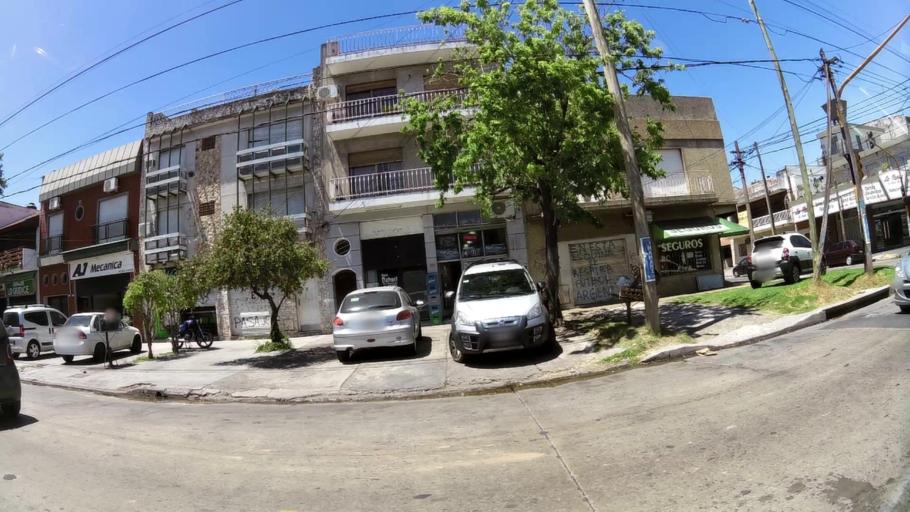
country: AR
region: Buenos Aires
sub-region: Partido de General San Martin
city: General San Martin
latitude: -34.5673
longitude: -58.5156
